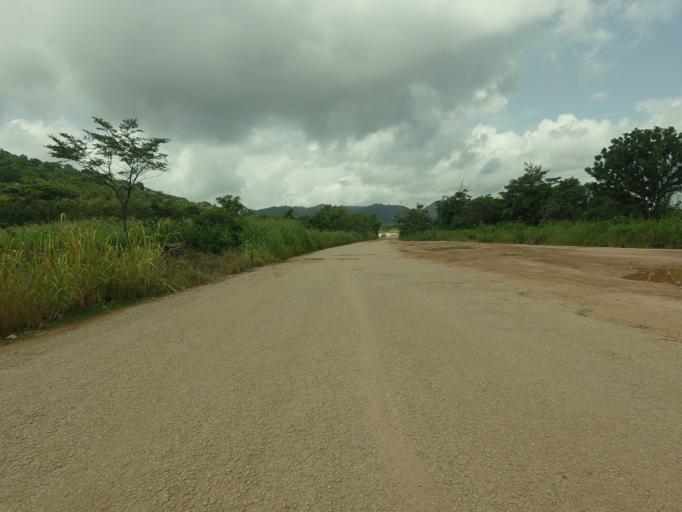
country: GH
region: Volta
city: Ho
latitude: 6.7018
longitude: 0.3352
